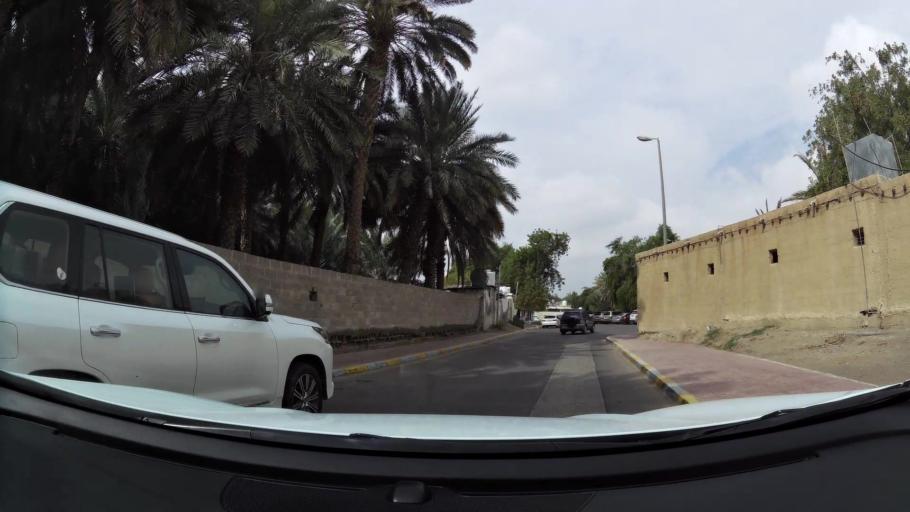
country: AE
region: Abu Dhabi
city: Al Ain
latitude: 24.2291
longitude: 55.7616
